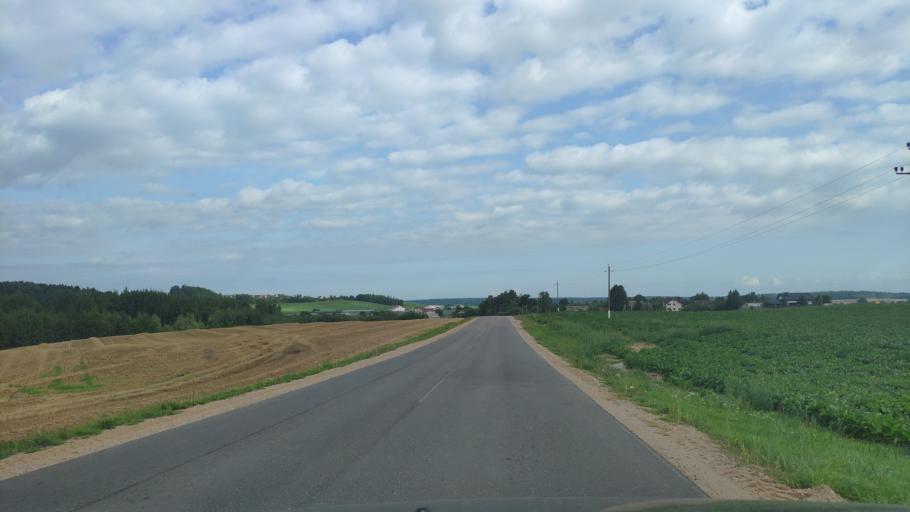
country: BY
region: Minsk
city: Khatsyezhyna
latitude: 53.8473
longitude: 27.3126
